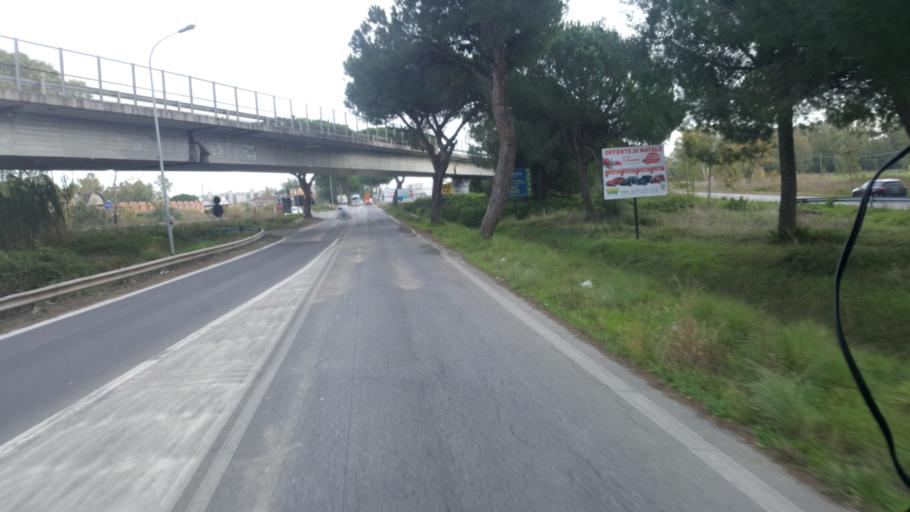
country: IT
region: Latium
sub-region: Provincia di Latina
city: Borgo Podgora
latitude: 41.4838
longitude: 12.8593
